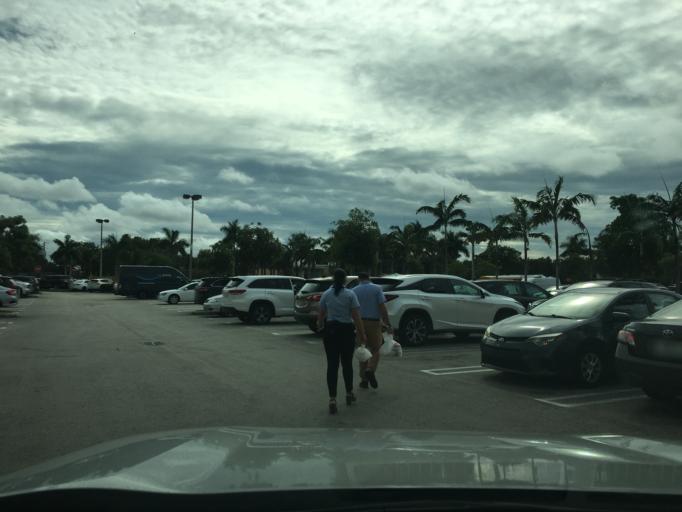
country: US
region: Florida
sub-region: Miami-Dade County
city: Palm Springs North
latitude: 25.9439
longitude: -80.3438
